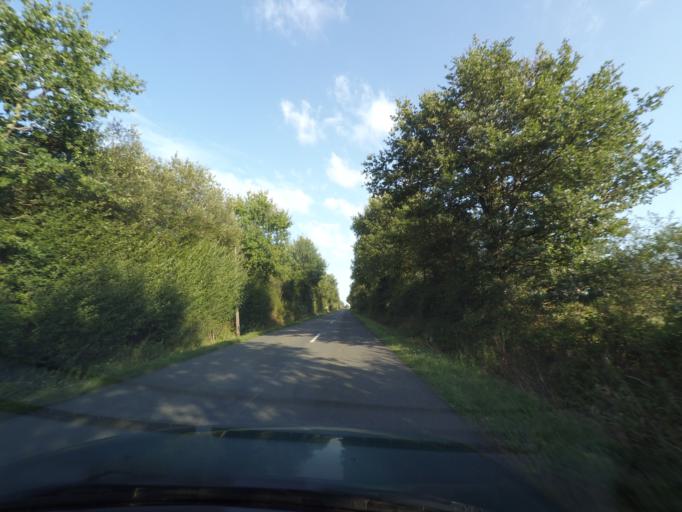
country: FR
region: Pays de la Loire
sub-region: Departement de la Loire-Atlantique
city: La Limouziniere
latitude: 47.0223
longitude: -1.6078
